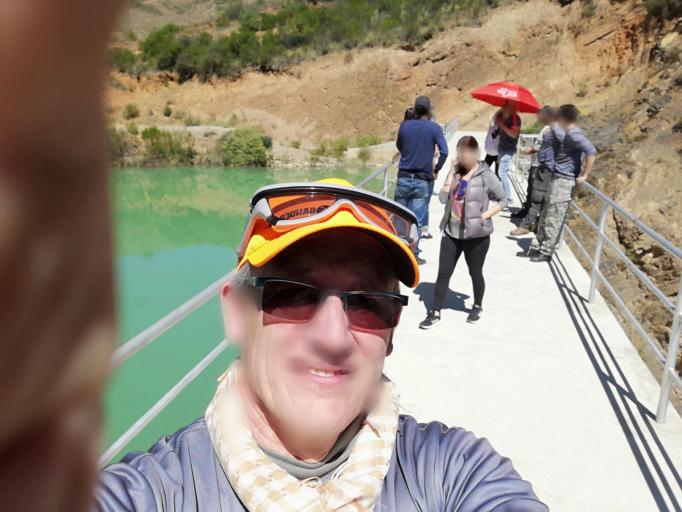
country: BO
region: Cochabamba
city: Tarata
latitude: -17.6583
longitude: -66.1292
